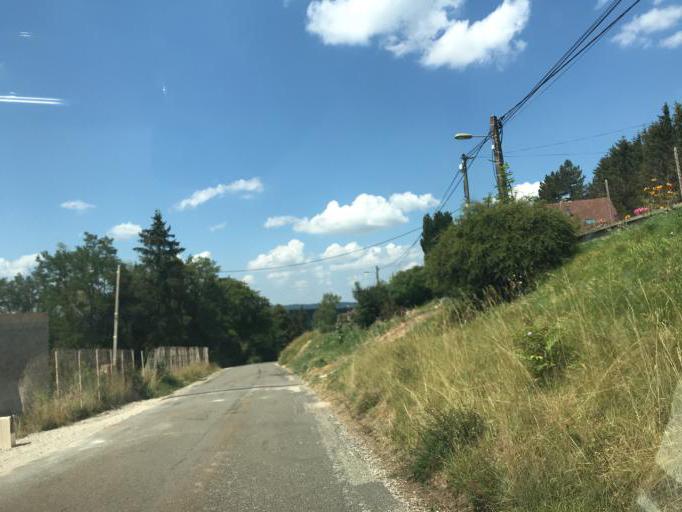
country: FR
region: Franche-Comte
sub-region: Departement du Jura
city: Clairvaux-les-Lacs
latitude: 46.5688
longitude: 5.7624
